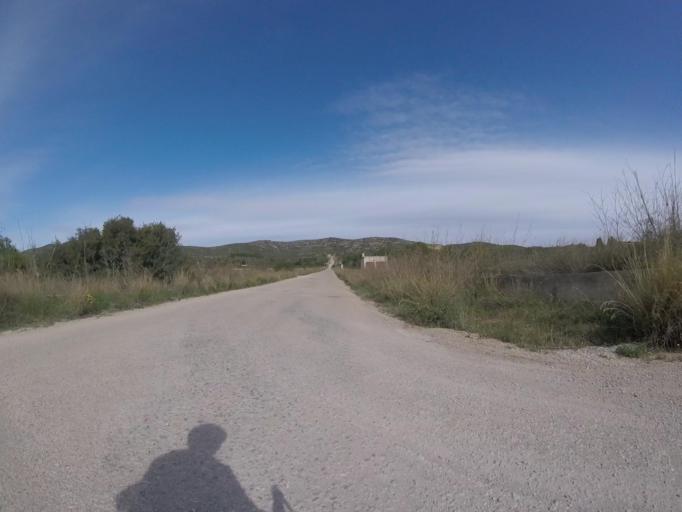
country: ES
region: Valencia
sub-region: Provincia de Castello
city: Torreblanca
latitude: 40.1997
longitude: 0.1669
